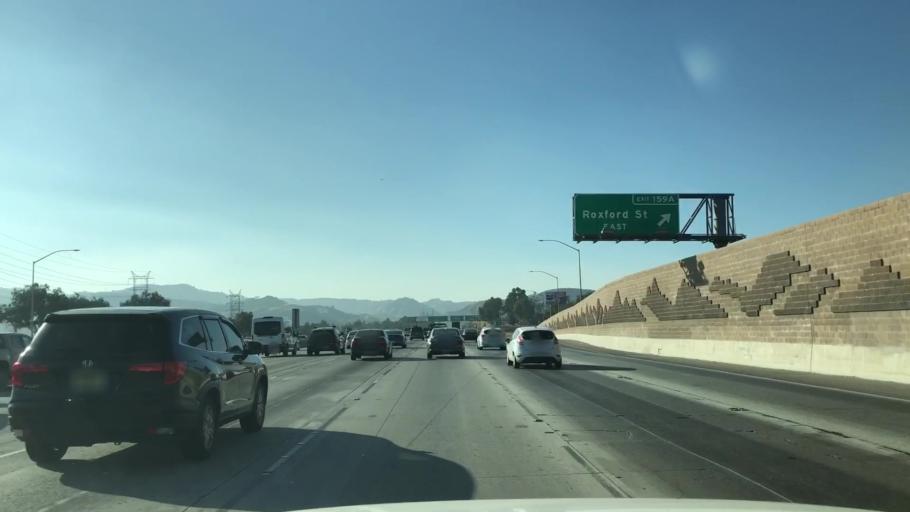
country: US
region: California
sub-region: Los Angeles County
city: San Fernando
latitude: 34.3009
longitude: -118.4763
